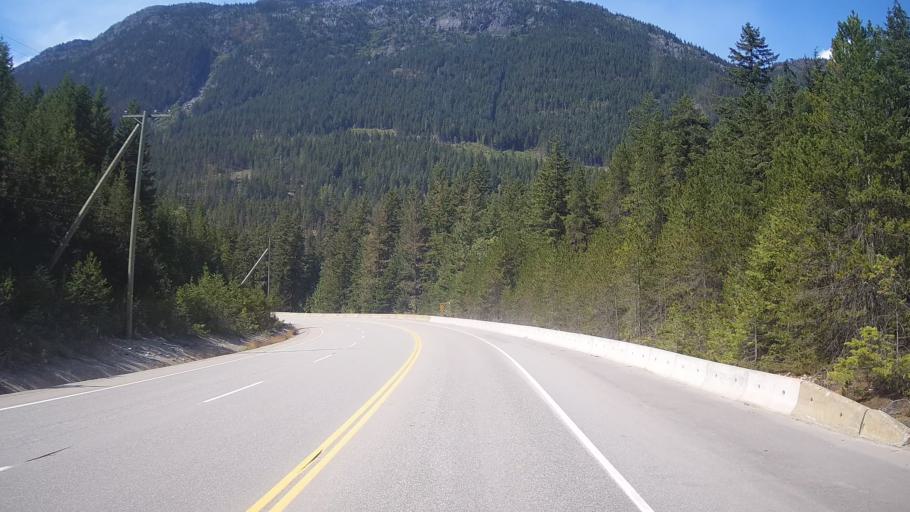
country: CA
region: British Columbia
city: Pemberton
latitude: 50.2196
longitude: -122.8836
